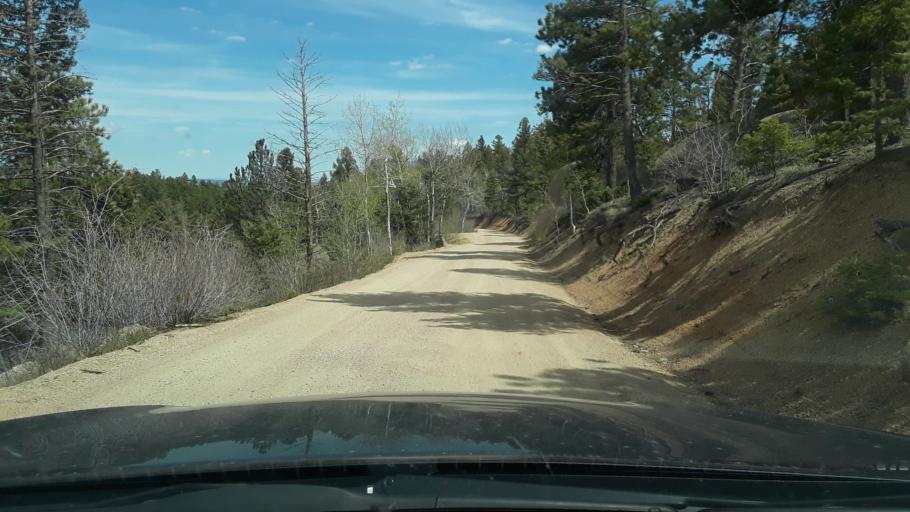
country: US
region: Colorado
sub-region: El Paso County
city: Palmer Lake
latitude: 39.0689
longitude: -104.9586
